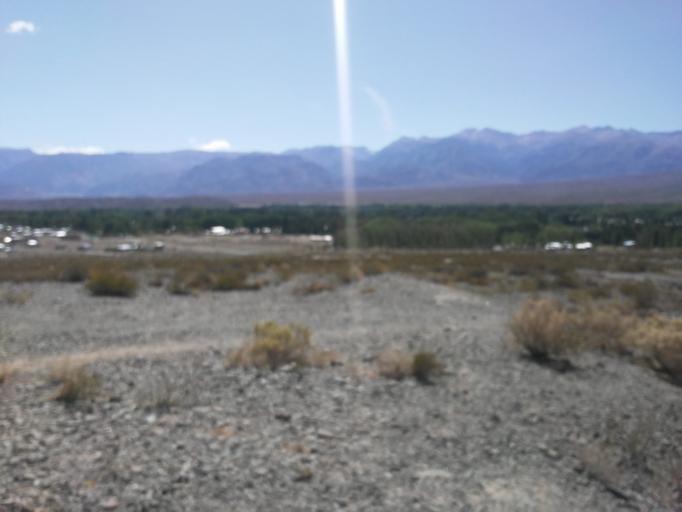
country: AR
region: Mendoza
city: Las Heras
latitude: -32.5954
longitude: -69.3297
